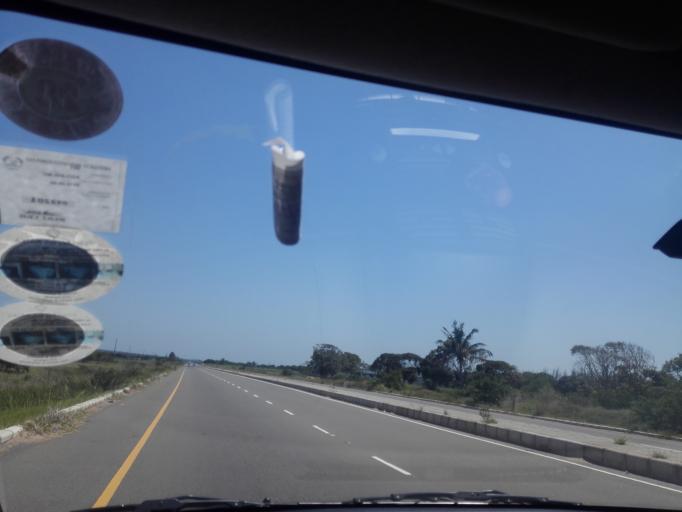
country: MZ
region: Maputo City
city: Maputo
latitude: -25.8018
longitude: 32.6731
